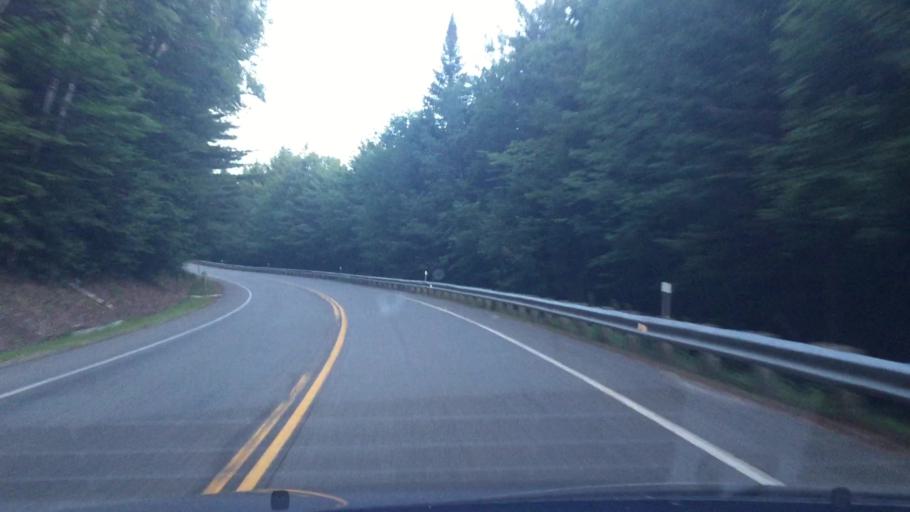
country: US
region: New Hampshire
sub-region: Grafton County
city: Woodstock
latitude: 44.0543
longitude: -71.5829
